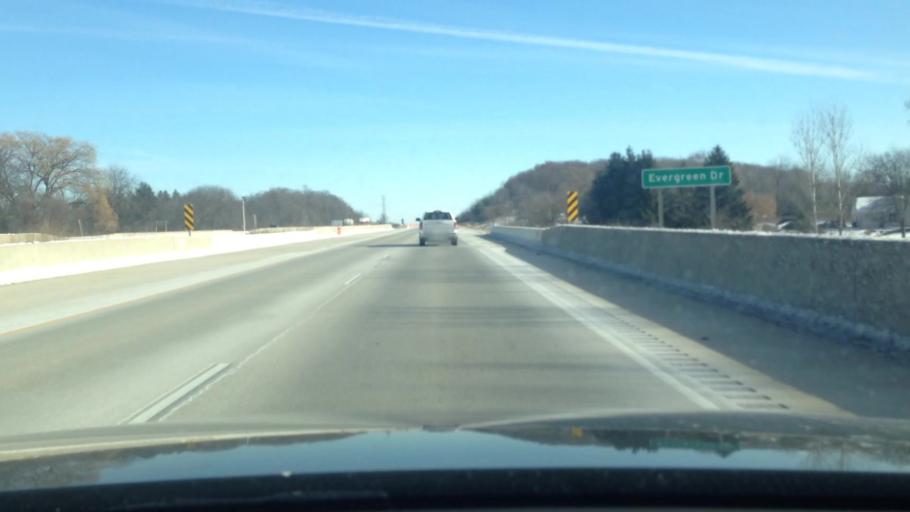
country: US
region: Wisconsin
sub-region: Waukesha County
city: Big Bend
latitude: 42.9054
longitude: -88.2368
